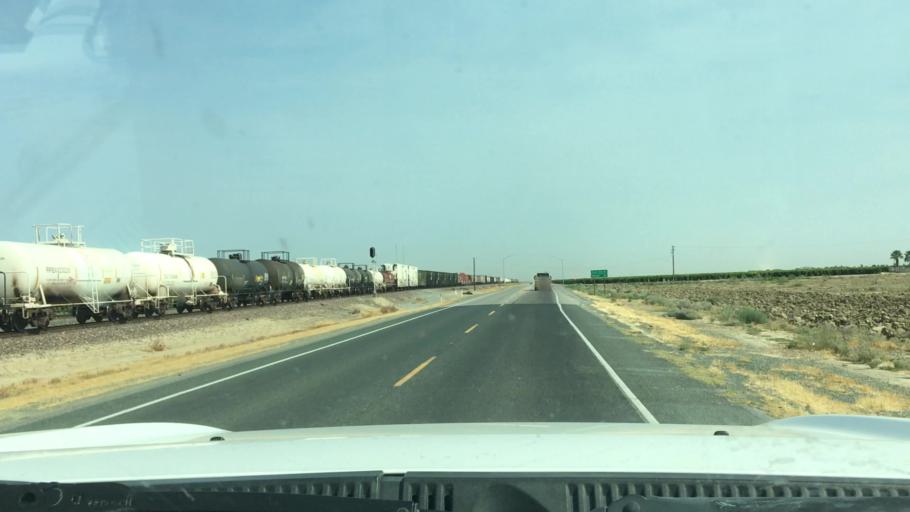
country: US
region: California
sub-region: Kern County
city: Delano
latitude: 35.7731
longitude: -119.3492
